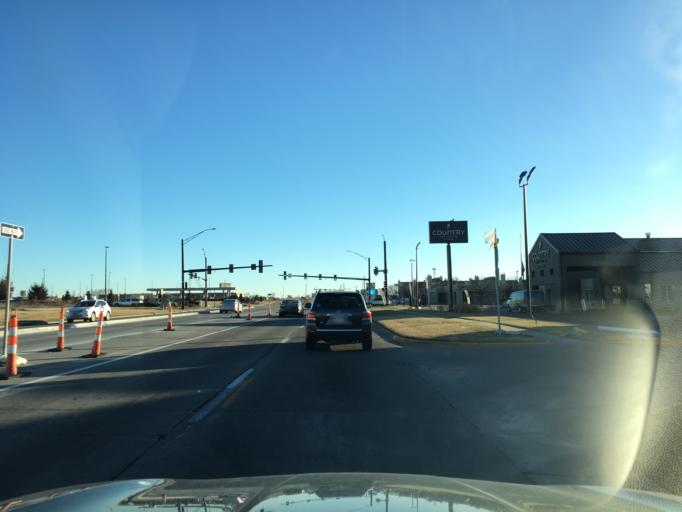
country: US
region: Kansas
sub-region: Sedgwick County
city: Bellaire
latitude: 37.6831
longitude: -97.2263
